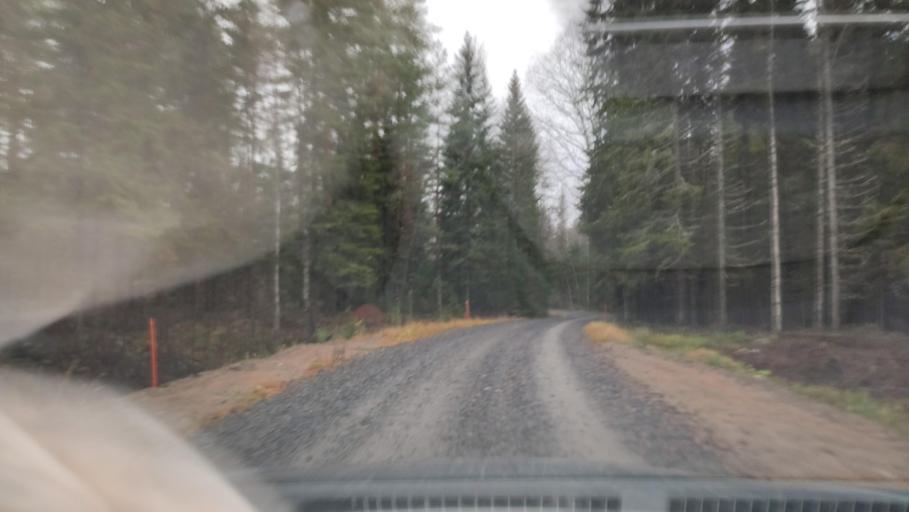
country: FI
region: Southern Ostrobothnia
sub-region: Suupohja
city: Karijoki
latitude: 62.1386
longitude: 21.6269
